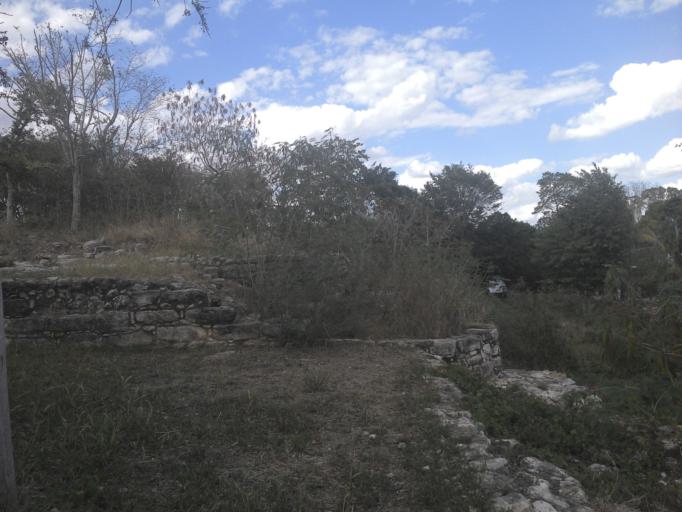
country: MX
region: Yucatan
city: Izamal
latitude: 20.9290
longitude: -89.0174
